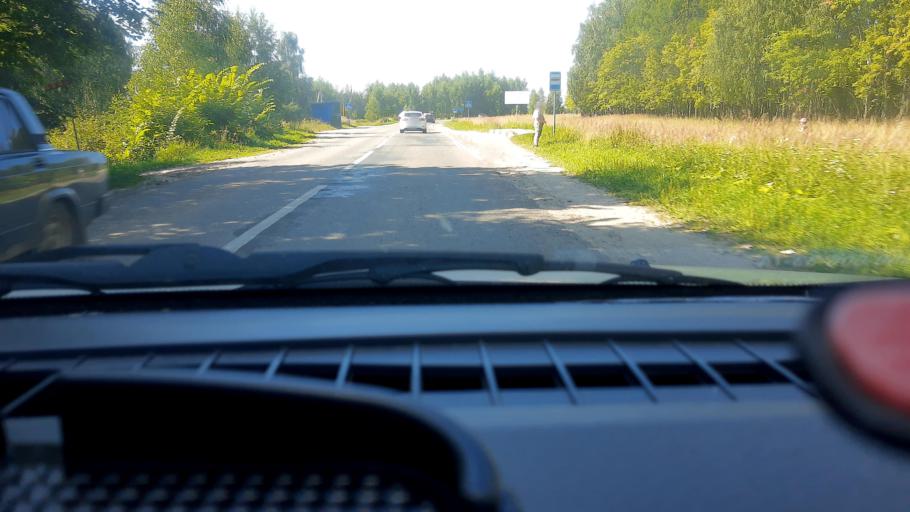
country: RU
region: Nizjnij Novgorod
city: Zavolzh'ye
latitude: 56.6916
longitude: 43.4204
